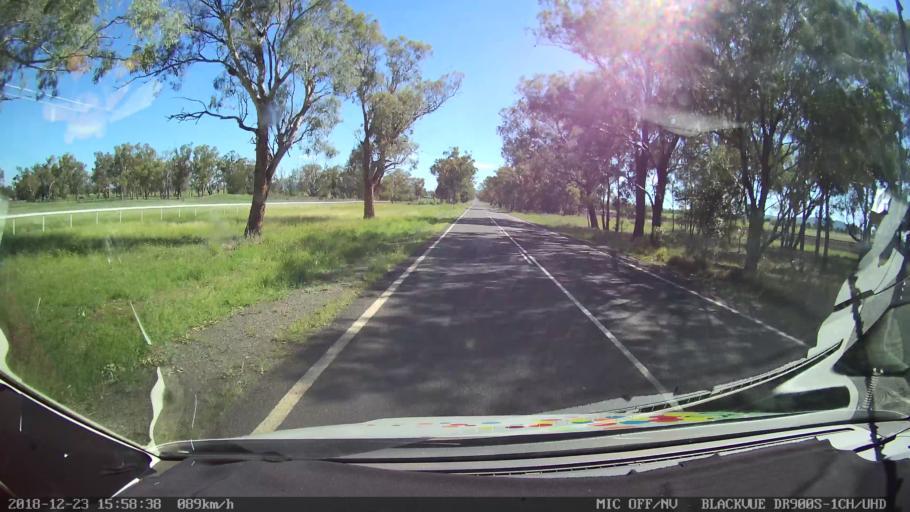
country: AU
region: New South Wales
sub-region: Tamworth Municipality
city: Phillip
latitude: -31.1905
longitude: 150.8401
